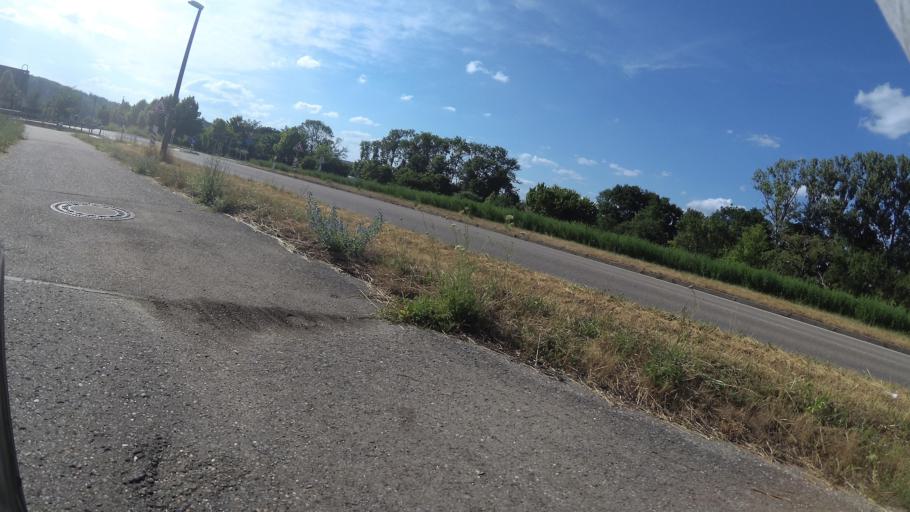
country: DE
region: Baden-Wuerttemberg
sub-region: Regierungsbezirk Stuttgart
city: Offenau
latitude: 49.2463
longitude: 9.1692
